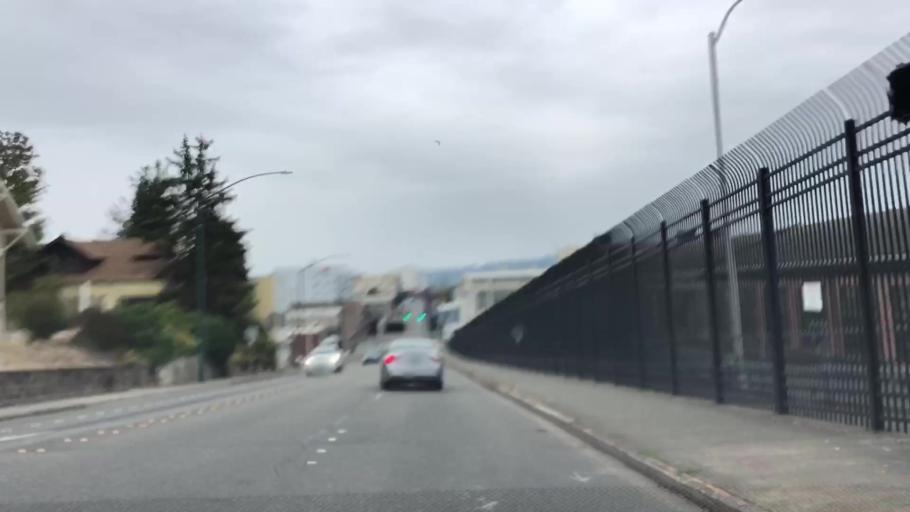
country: US
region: Washington
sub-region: Kitsap County
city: Bremerton
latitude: 47.5650
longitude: -122.6328
